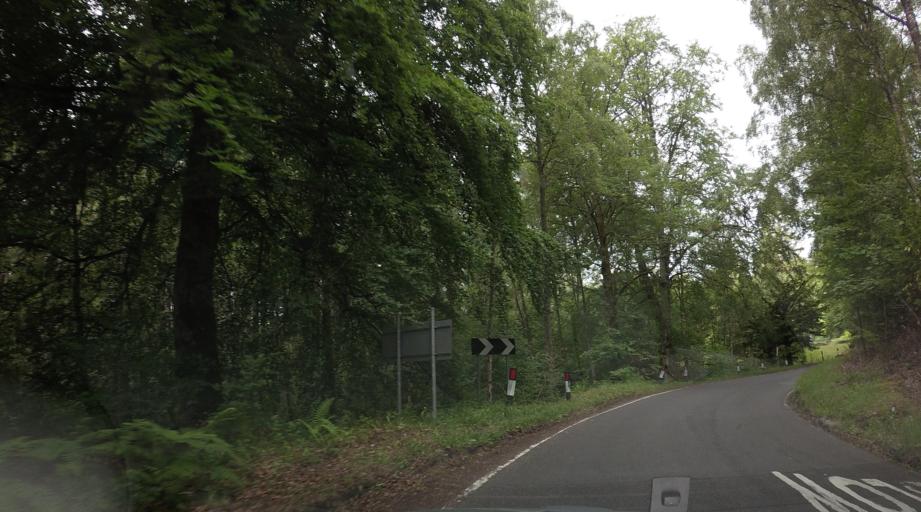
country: GB
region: Scotland
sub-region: Perth and Kinross
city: Pitlochry
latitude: 56.7285
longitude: -3.8032
